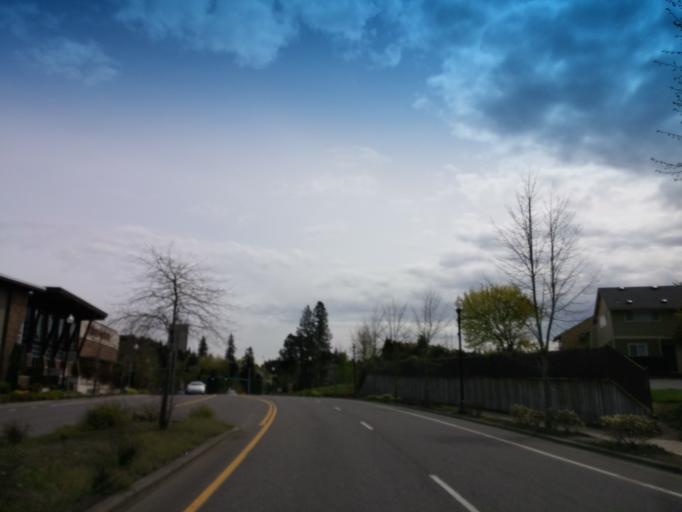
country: US
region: Oregon
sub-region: Washington County
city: Cedar Mill
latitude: 45.5206
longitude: -122.8031
